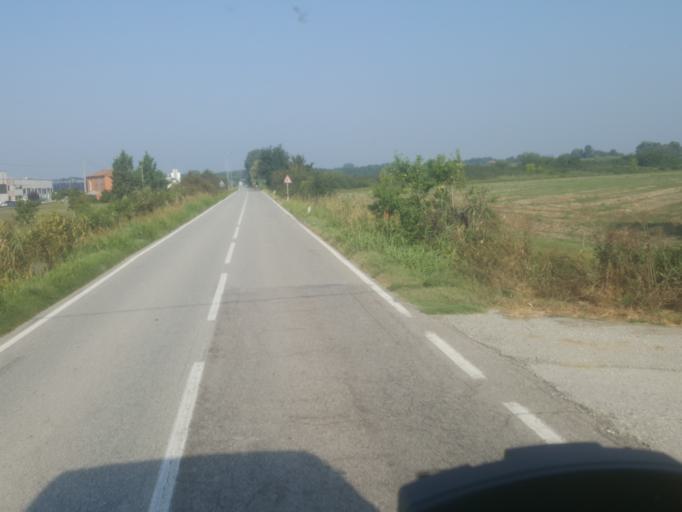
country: IT
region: Emilia-Romagna
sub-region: Provincia di Ravenna
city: Lavezzola
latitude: 44.5703
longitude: 11.8883
